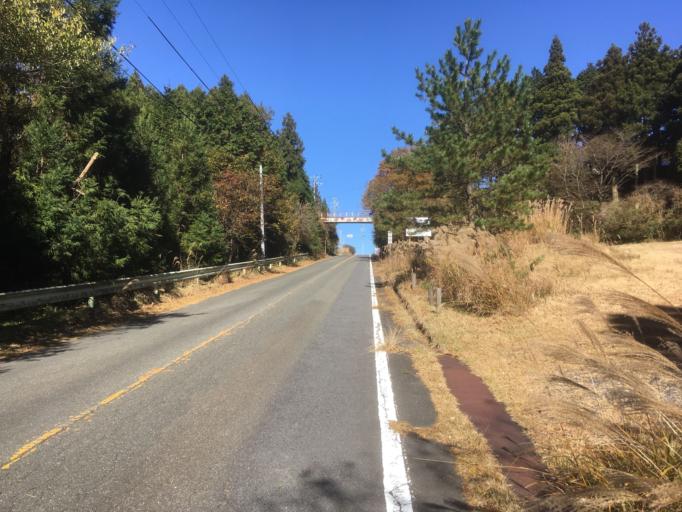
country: JP
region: Mie
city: Ueno-ebisumachi
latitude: 34.6880
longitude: 136.2750
